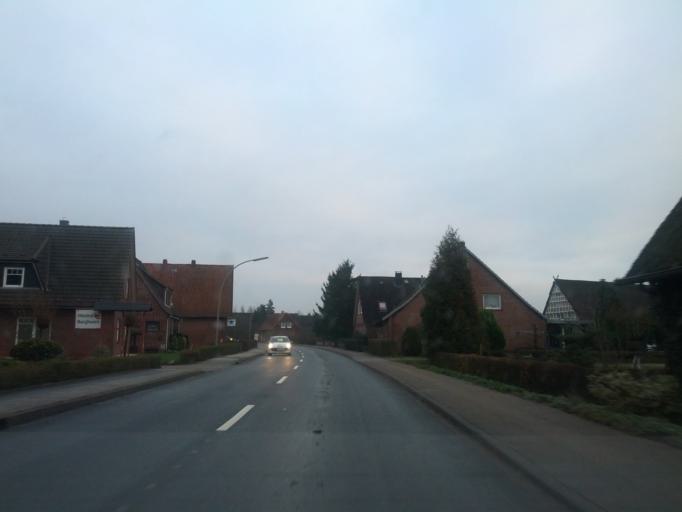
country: DE
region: Lower Saxony
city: Neu Wulmstorf
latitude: 53.5166
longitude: 9.7856
